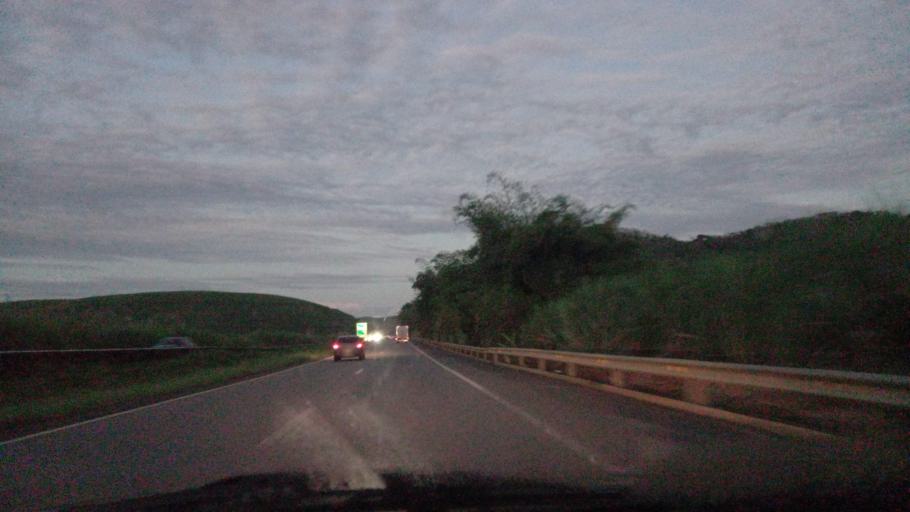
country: BR
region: Pernambuco
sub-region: Escada
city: Escada
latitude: -8.4106
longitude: -35.2904
